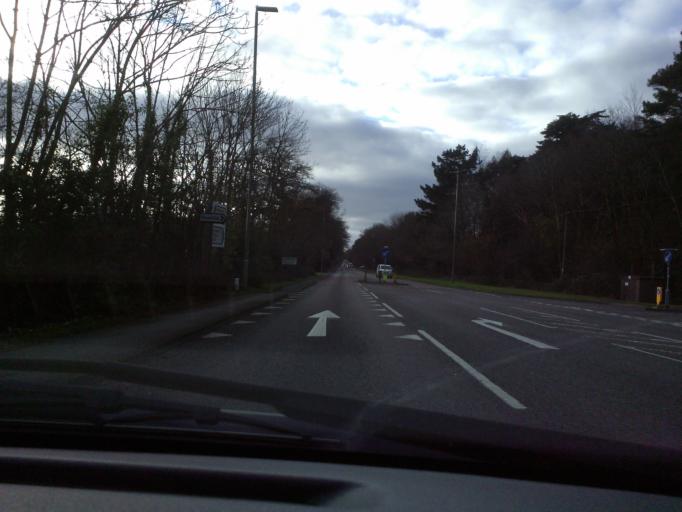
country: GB
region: England
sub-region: Hampshire
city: Totton
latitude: 50.8978
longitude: -1.5093
